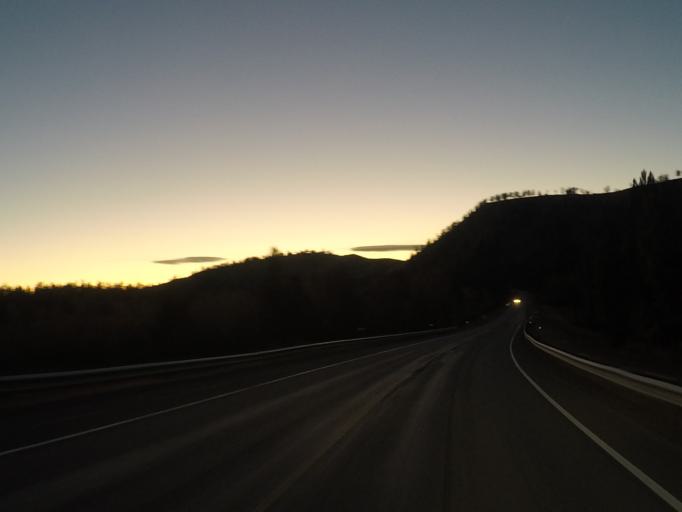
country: US
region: Montana
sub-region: Missoula County
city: Seeley Lake
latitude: 47.0225
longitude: -113.2946
